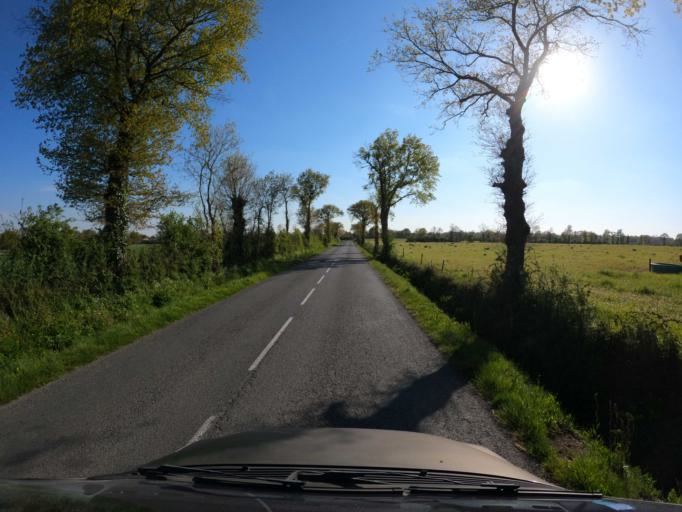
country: FR
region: Pays de la Loire
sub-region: Departement de la Vendee
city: Beaurepaire
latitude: 46.9267
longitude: -1.1143
